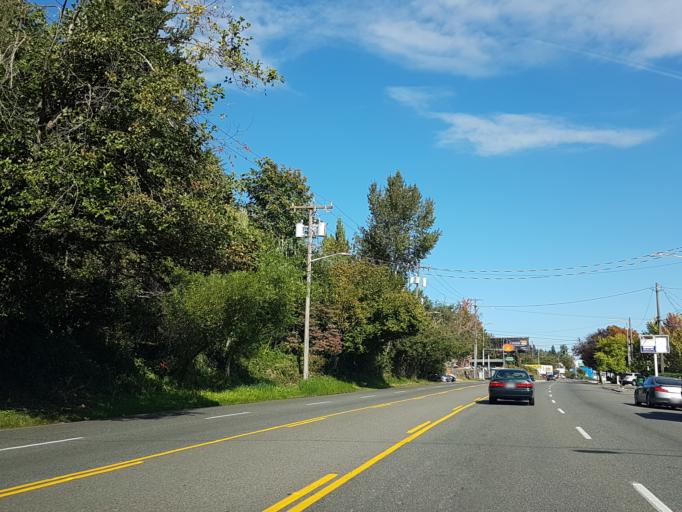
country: US
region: Washington
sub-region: King County
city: Lake Forest Park
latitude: 47.7071
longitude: -122.3016
